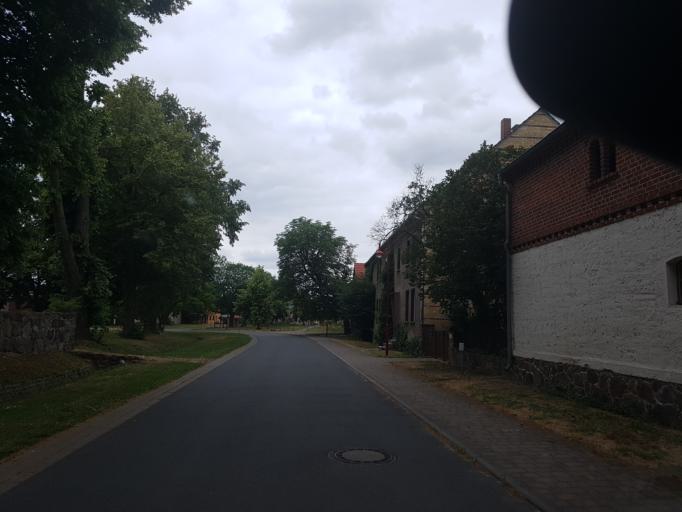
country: DE
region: Saxony-Anhalt
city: Seyda
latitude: 51.9527
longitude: 12.9134
